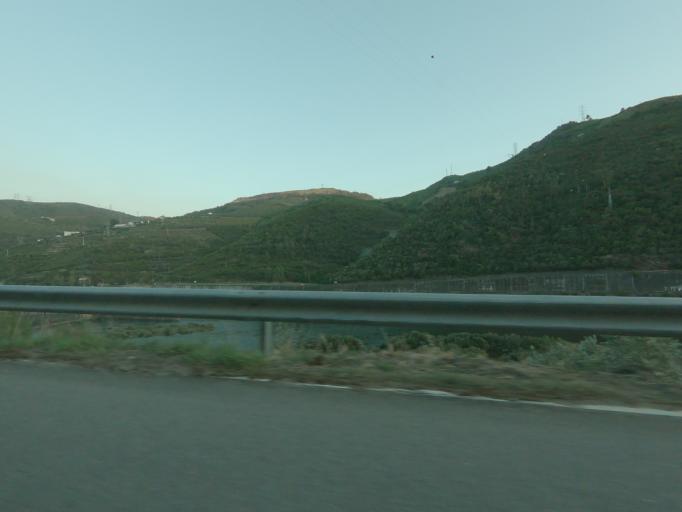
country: PT
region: Vila Real
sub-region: Peso da Regua
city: Peso da Regua
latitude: 41.1488
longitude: -7.7445
